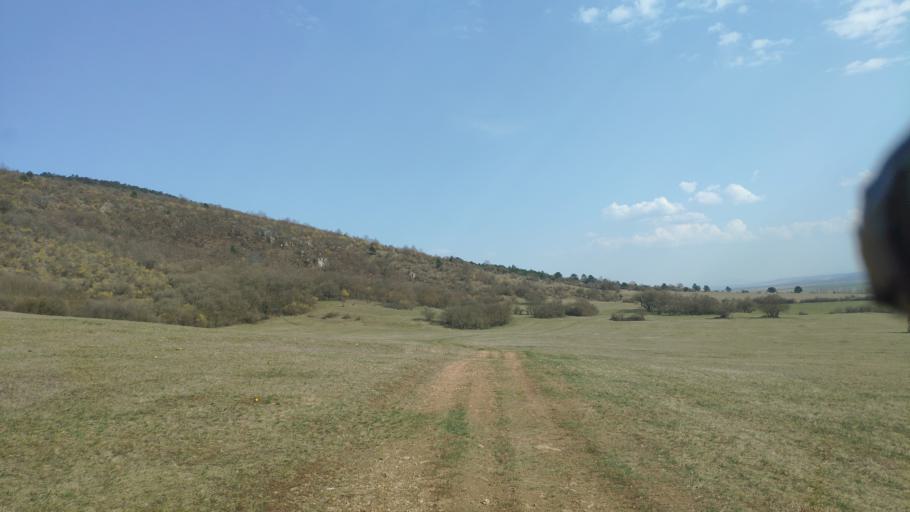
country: SK
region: Kosicky
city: Medzev
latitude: 48.6237
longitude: 20.9013
